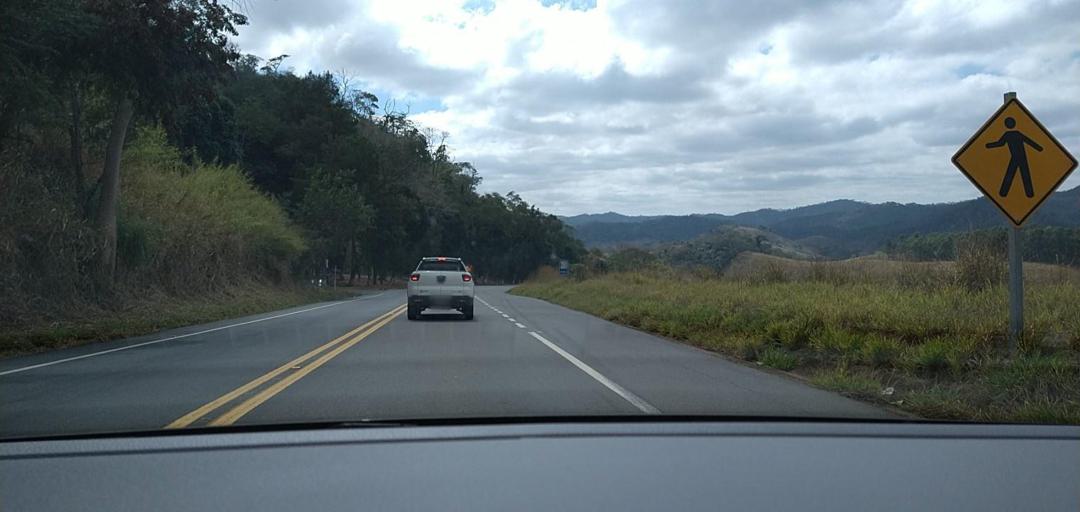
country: BR
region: Minas Gerais
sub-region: Ponte Nova
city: Ponte Nova
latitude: -20.5107
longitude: -42.8841
